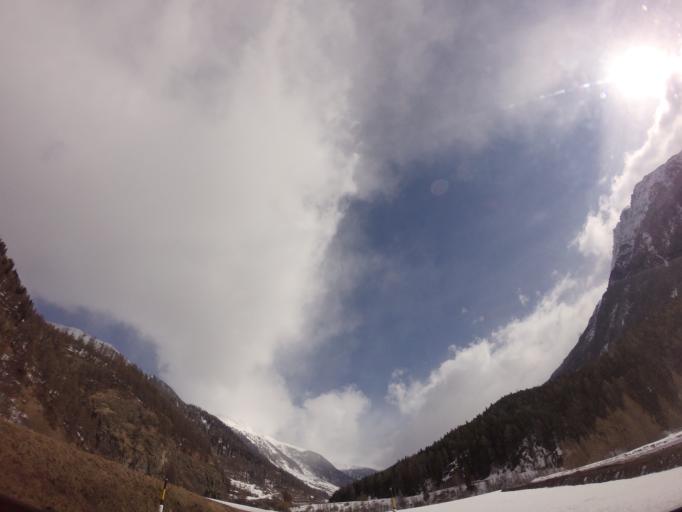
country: CH
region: Grisons
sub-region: Inn District
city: Zernez
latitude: 46.7566
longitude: 10.0866
